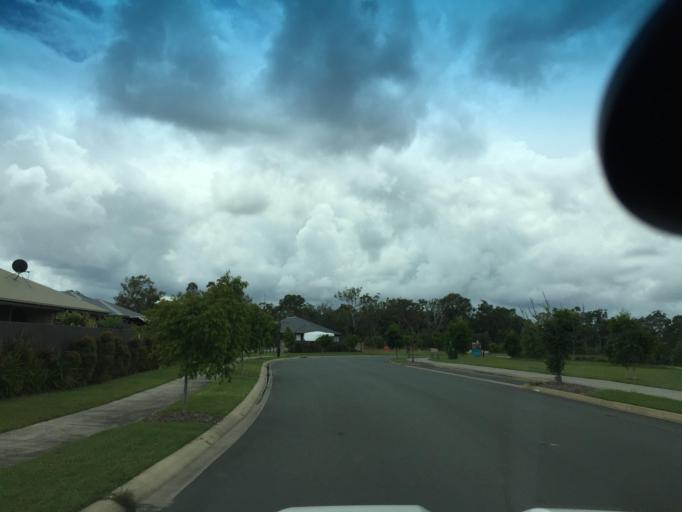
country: AU
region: Queensland
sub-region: Moreton Bay
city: Caboolture
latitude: -27.0614
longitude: 152.9301
